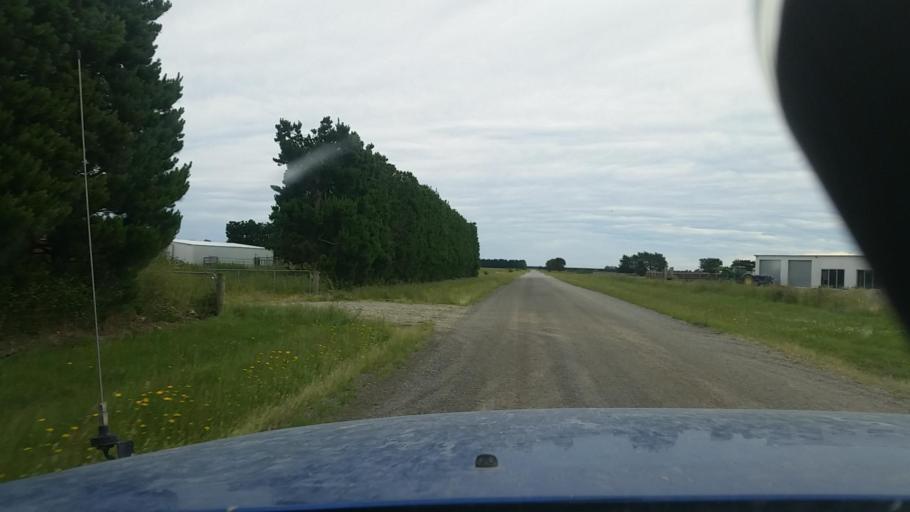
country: NZ
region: Canterbury
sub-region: Ashburton District
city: Tinwald
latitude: -43.9327
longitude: 171.6076
